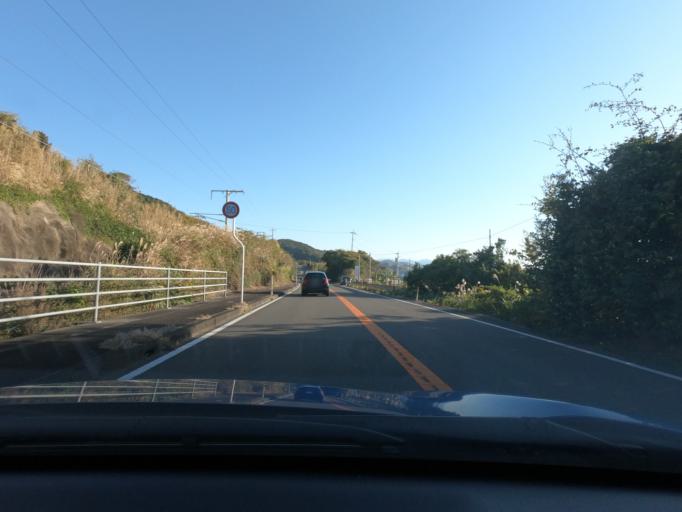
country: JP
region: Kagoshima
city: Akune
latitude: 31.9371
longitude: 130.2178
